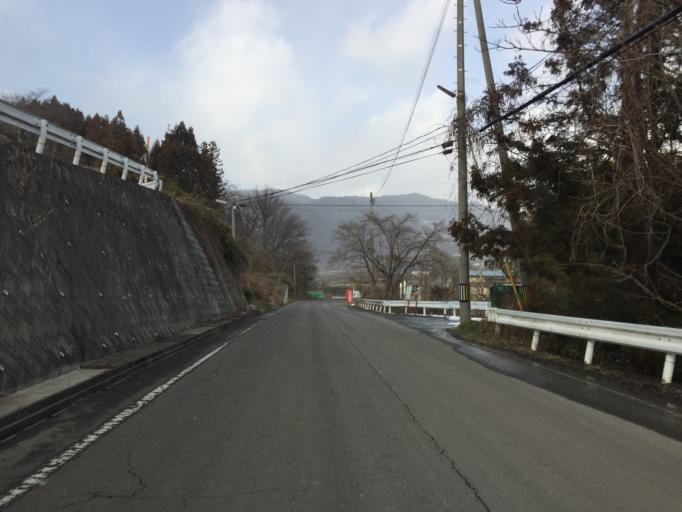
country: JP
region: Fukushima
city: Fukushima-shi
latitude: 37.8372
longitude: 140.4562
